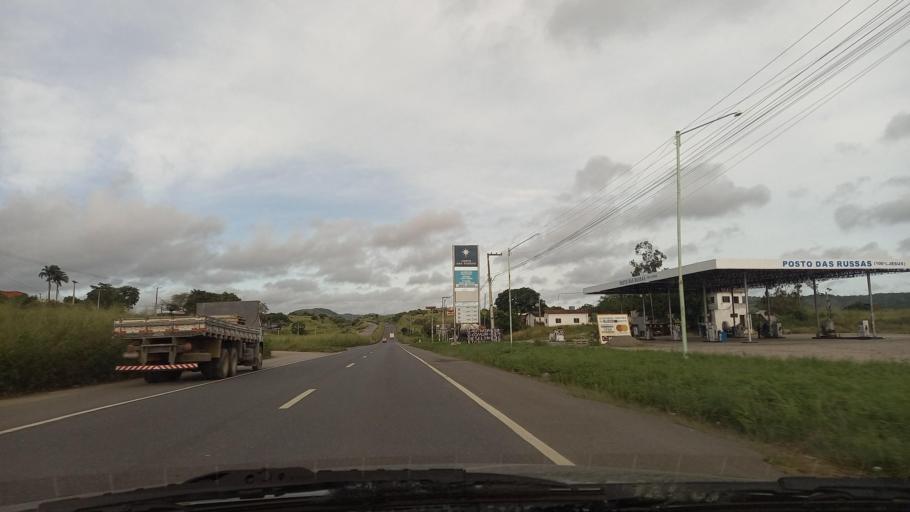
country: BR
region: Pernambuco
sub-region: Pombos
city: Pombos
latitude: -8.1296
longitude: -35.3584
